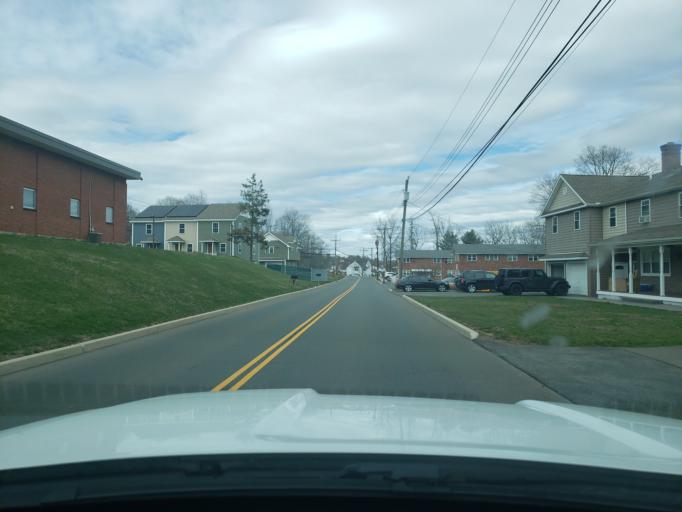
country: US
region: Connecticut
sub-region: Middlesex County
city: Middletown
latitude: 41.5352
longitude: -72.6549
